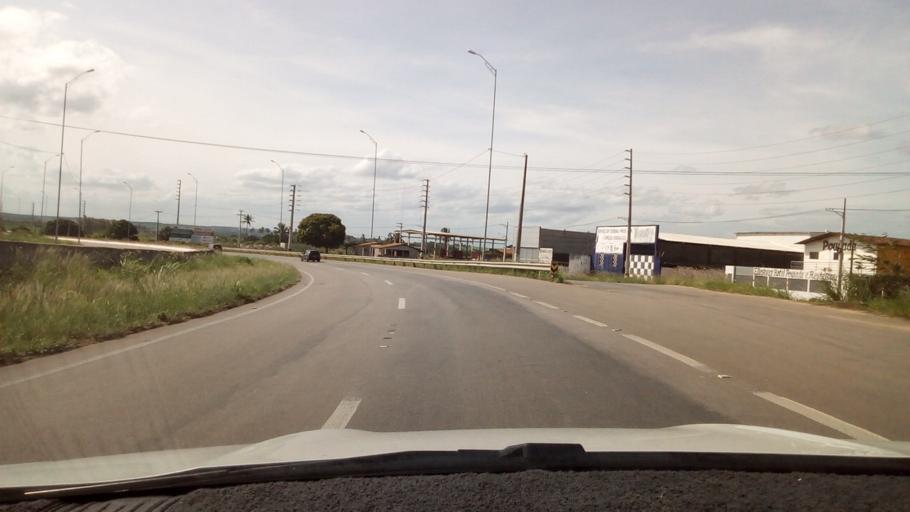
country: BR
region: Paraiba
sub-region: Bayeux
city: Bayeux
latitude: -7.1174
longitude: -34.9495
